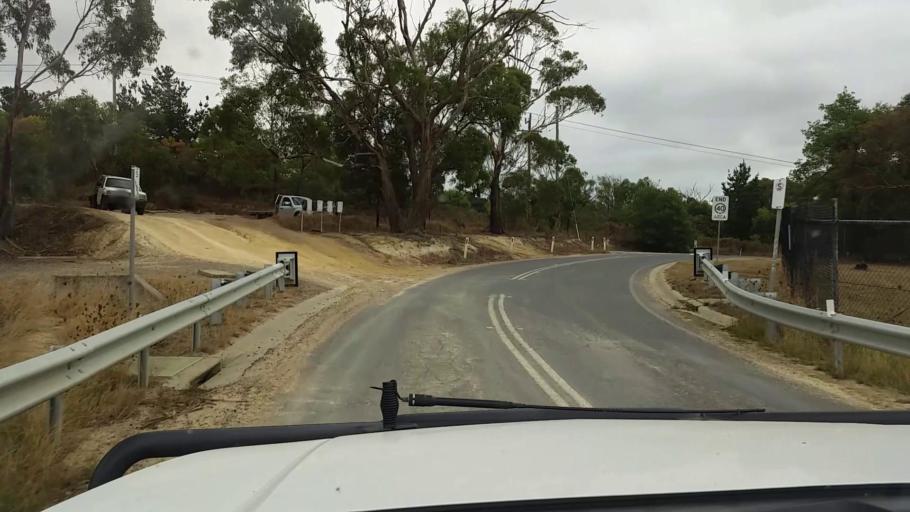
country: AU
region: Victoria
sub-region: Mornington Peninsula
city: Moorooduc
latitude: -38.2779
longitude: 145.0987
